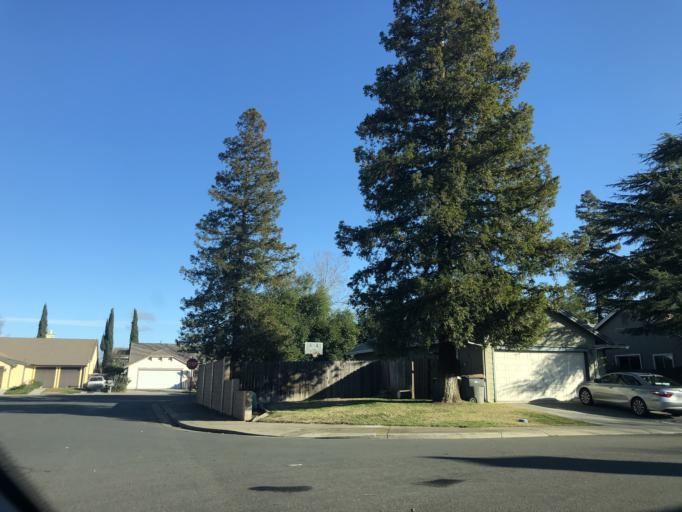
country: US
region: California
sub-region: Yolo County
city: Woodland
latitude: 38.6654
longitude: -121.7479
